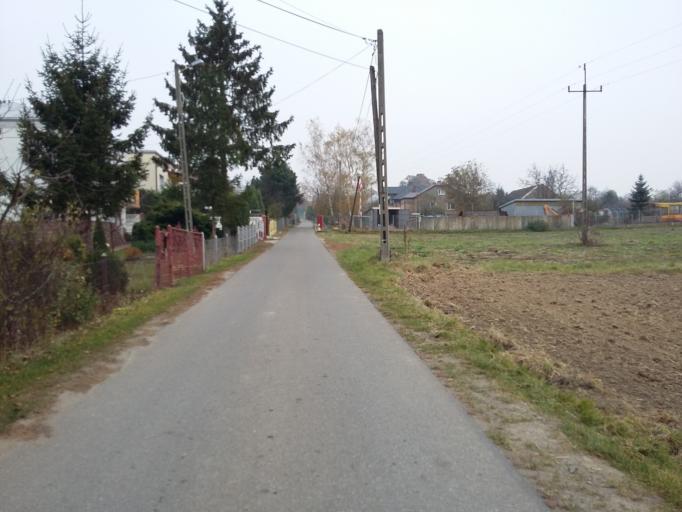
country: PL
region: Subcarpathian Voivodeship
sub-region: Powiat jasielski
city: Tarnowiec
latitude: 49.7319
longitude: 21.5722
